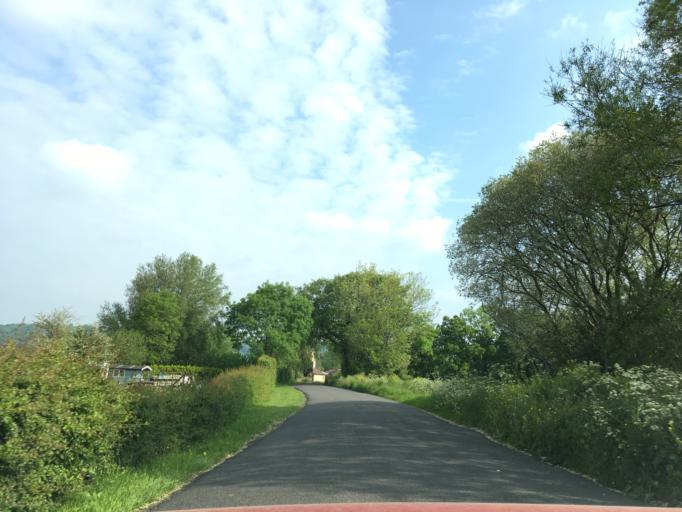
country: GB
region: England
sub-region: North Somerset
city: Nailsea
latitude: 51.4320
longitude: -2.7809
